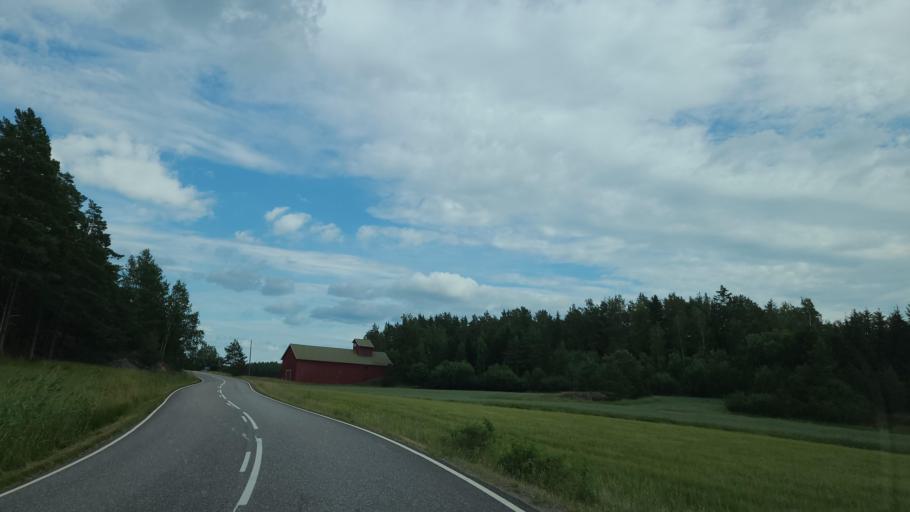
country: FI
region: Varsinais-Suomi
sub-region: Turku
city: Rymaettylae
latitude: 60.3545
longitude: 21.9547
